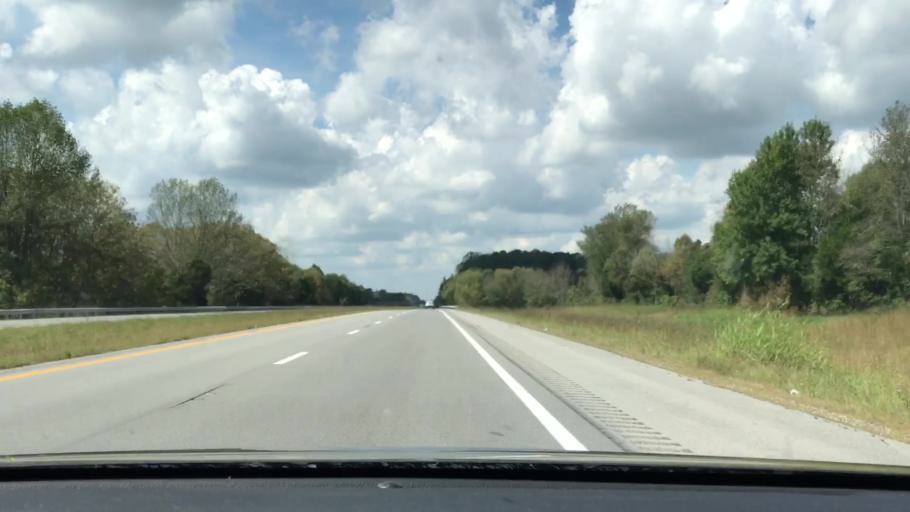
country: US
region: Kentucky
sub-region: Adair County
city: Columbia
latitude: 37.0692
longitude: -85.2093
